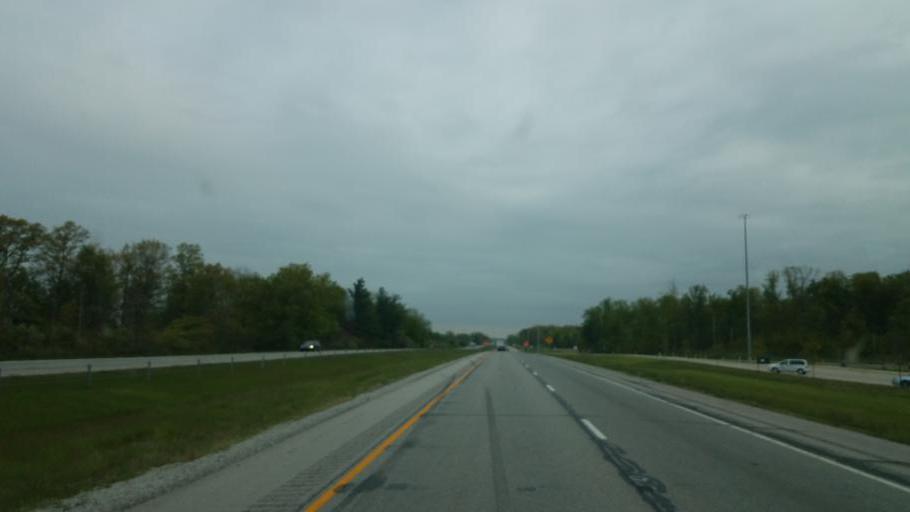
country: US
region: Indiana
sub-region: DeKalb County
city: Garrett
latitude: 41.2957
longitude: -85.0873
